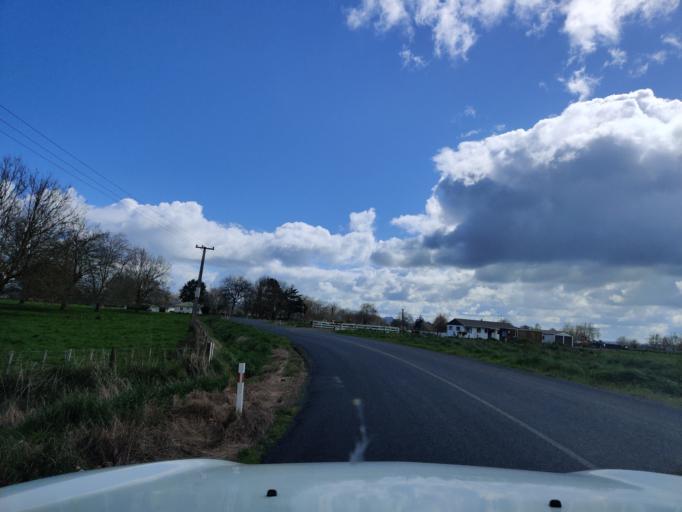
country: NZ
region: Waikato
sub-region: Waikato District
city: Ngaruawahia
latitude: -37.6170
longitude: 175.3165
